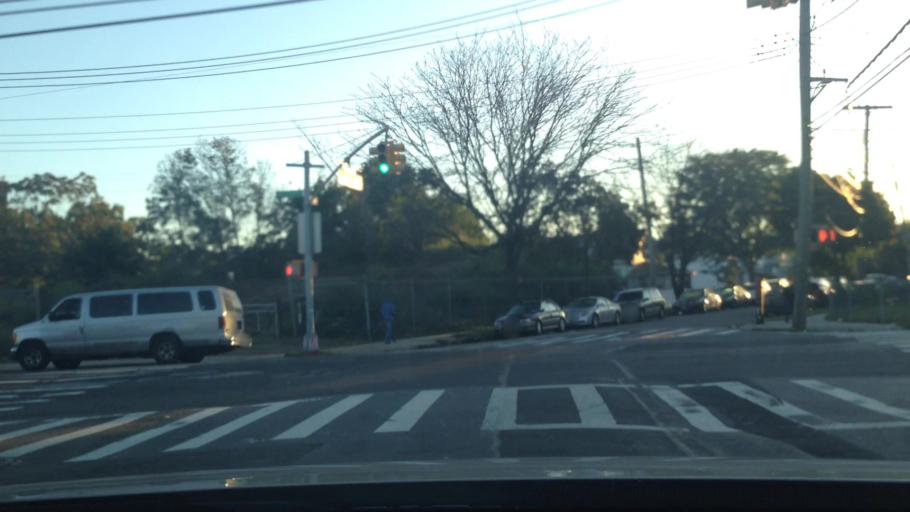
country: US
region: New York
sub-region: Queens County
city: Jamaica
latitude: 40.6706
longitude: -73.7739
